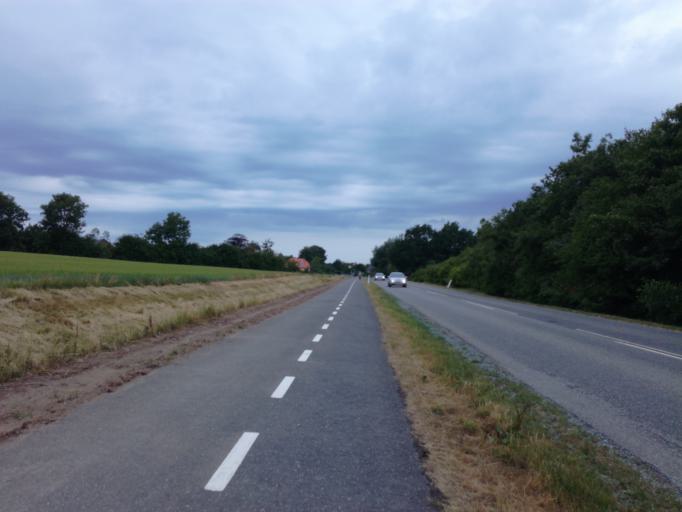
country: DK
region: South Denmark
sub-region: Vejle Kommune
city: Borkop
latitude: 55.6648
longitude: 9.6269
